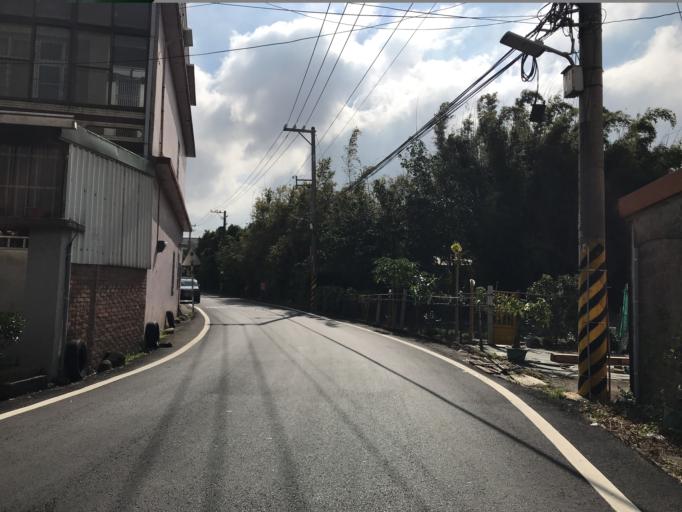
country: TW
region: Taiwan
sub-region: Hsinchu
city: Zhubei
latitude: 24.8106
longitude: 121.0026
